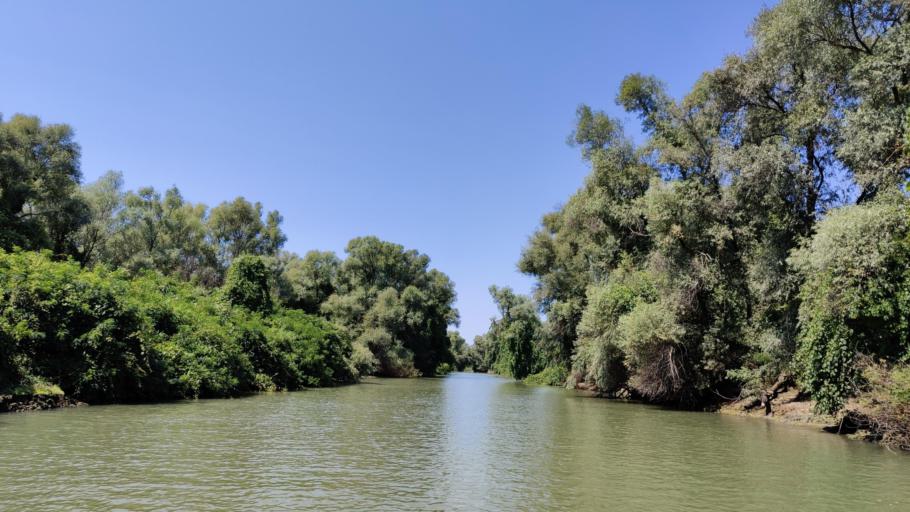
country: RO
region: Tulcea
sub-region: Comuna Pardina
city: Pardina
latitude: 45.2546
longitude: 28.9448
